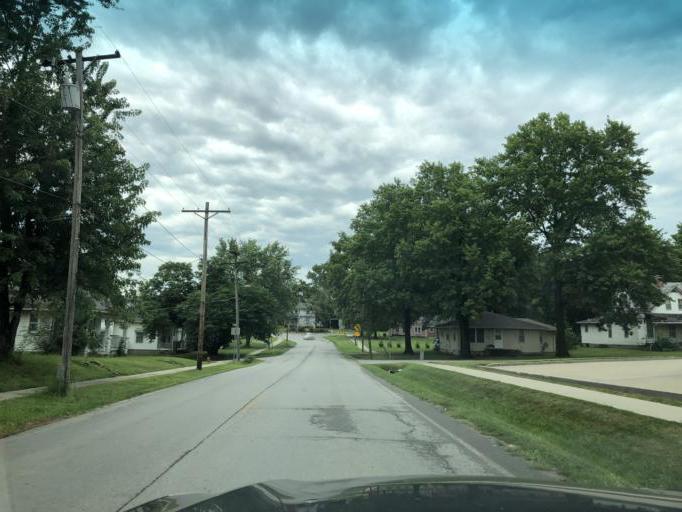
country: US
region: Missouri
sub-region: Saline County
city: Sweet Springs
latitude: 38.9673
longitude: -93.4150
